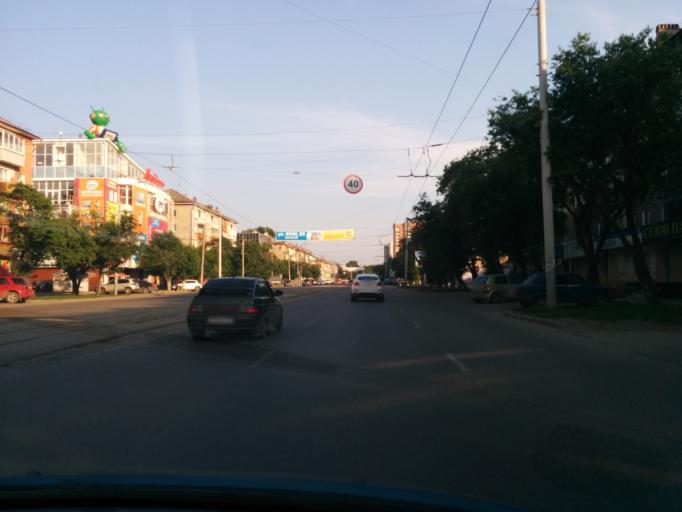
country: RU
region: Perm
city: Perm
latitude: 58.0177
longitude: 56.2786
